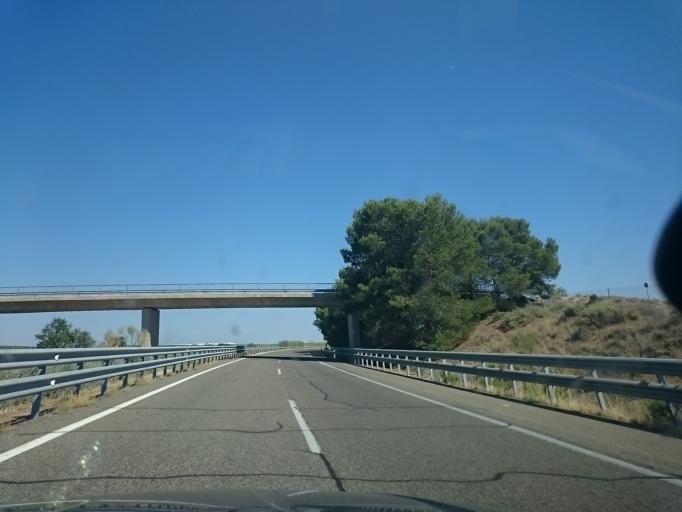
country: ES
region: Aragon
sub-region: Provincia de Huesca
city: Candasnos
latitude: 41.5039
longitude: 0.1080
